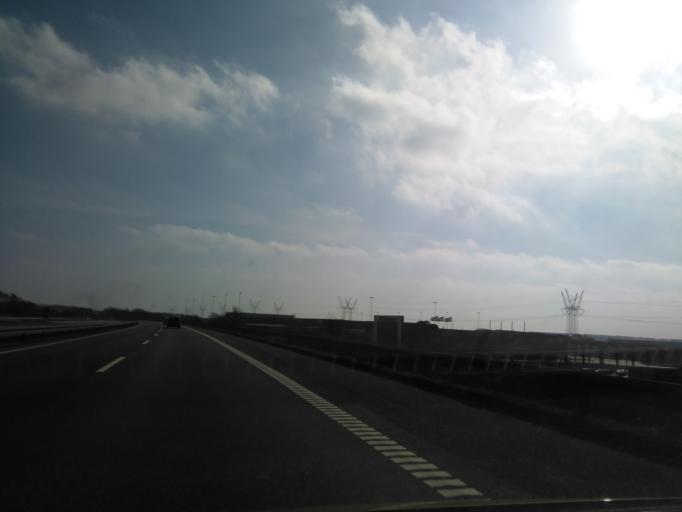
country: DK
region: South Denmark
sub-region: Fredericia Kommune
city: Taulov
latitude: 55.5438
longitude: 9.6479
